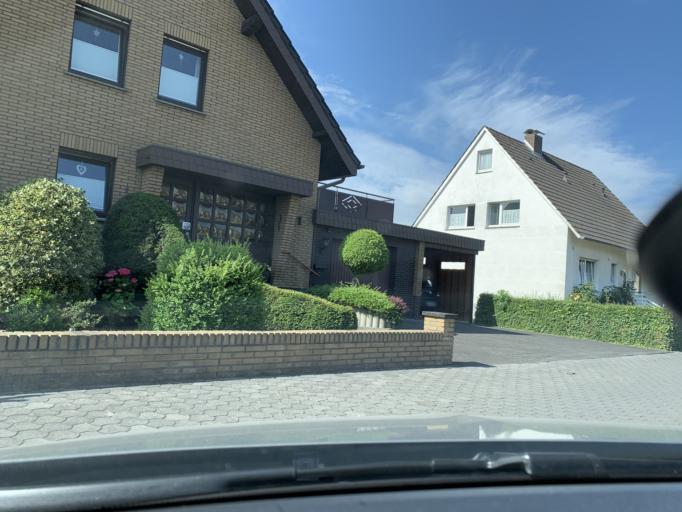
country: DE
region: North Rhine-Westphalia
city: Geseke
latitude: 51.6870
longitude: 8.4366
